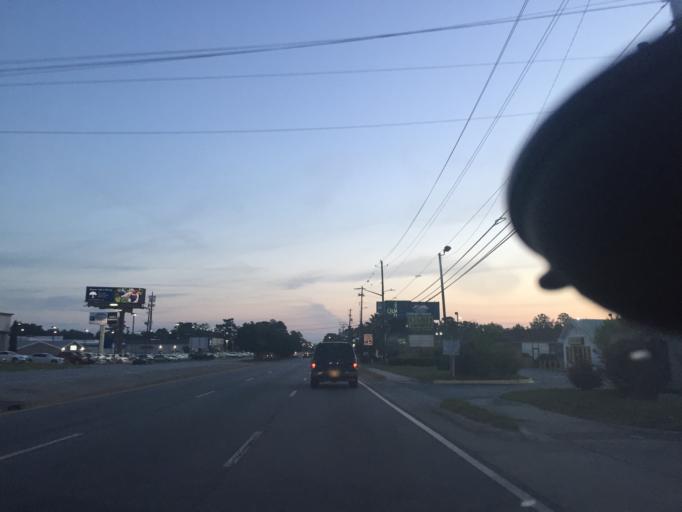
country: US
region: Georgia
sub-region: Chatham County
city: Isle of Hope
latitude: 32.0106
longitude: -81.1142
